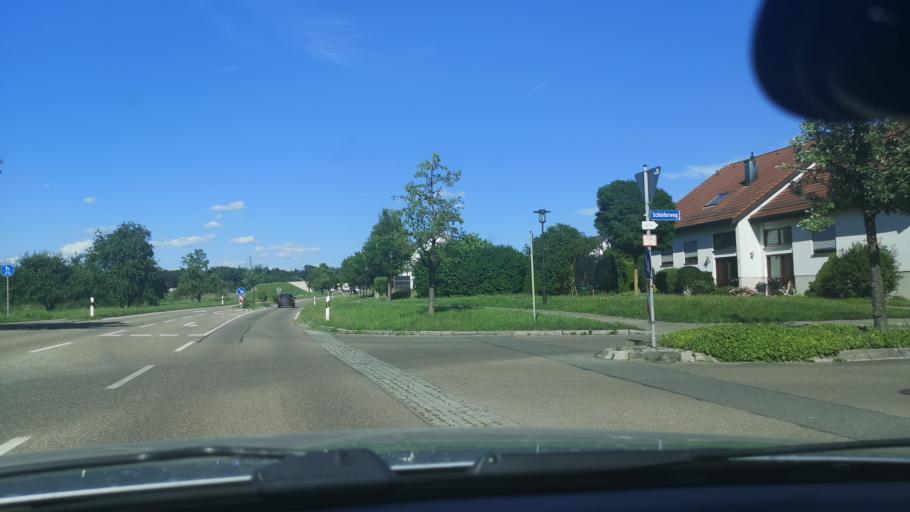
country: DE
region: Baden-Wuerttemberg
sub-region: Regierungsbezirk Stuttgart
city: Ohmden
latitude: 48.6486
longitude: 9.5336
